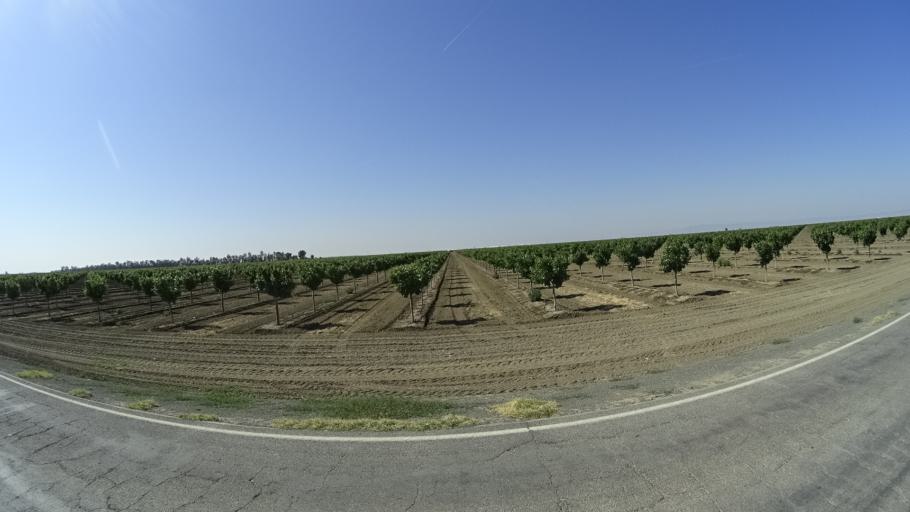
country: US
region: California
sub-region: Fresno County
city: Riverdale
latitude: 36.3864
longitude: -119.9445
